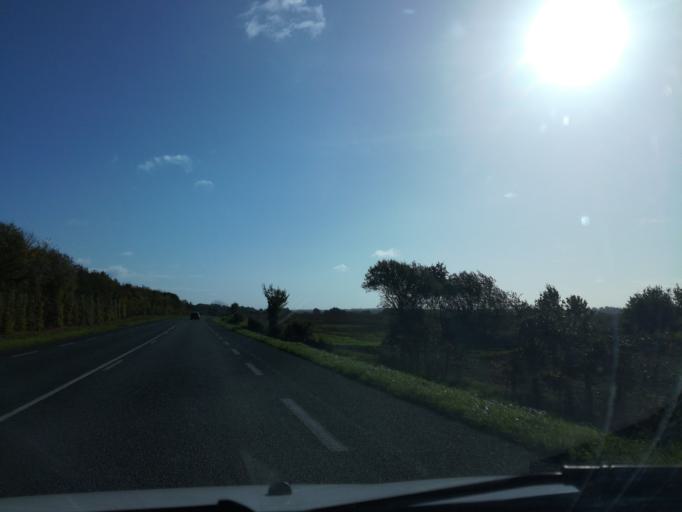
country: FR
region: Pays de la Loire
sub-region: Departement de Maine-et-Loire
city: Pouance
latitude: 47.7682
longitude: -1.2228
